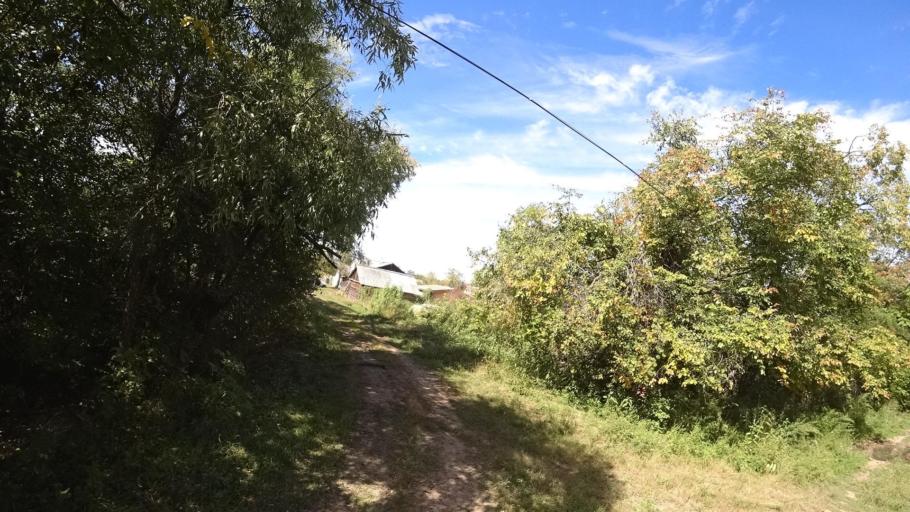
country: RU
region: Primorskiy
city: Yakovlevka
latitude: 44.4290
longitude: 133.5738
